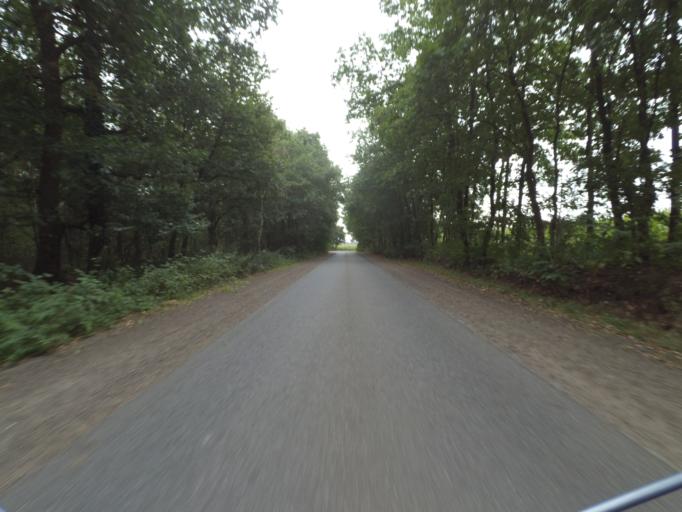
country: NL
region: Overijssel
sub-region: Gemeente Losser
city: Losser
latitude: 52.2766
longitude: 7.0497
